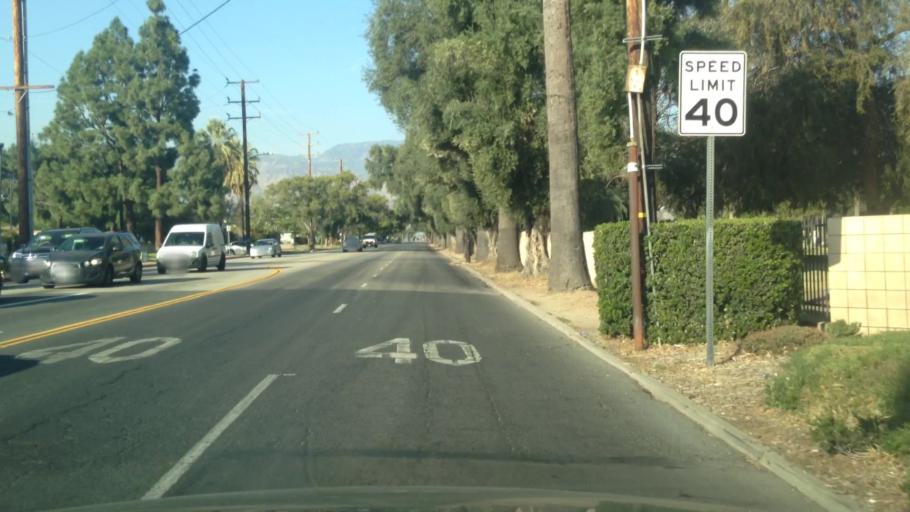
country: US
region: California
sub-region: San Bernardino County
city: San Bernardino
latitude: 34.1361
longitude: -117.2787
